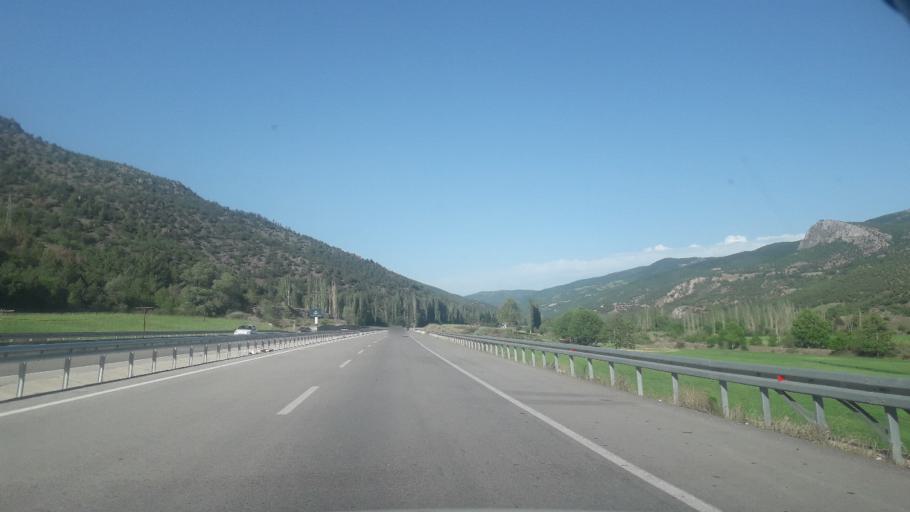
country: TR
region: Tokat
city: Turhal
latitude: 40.4723
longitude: 36.1332
